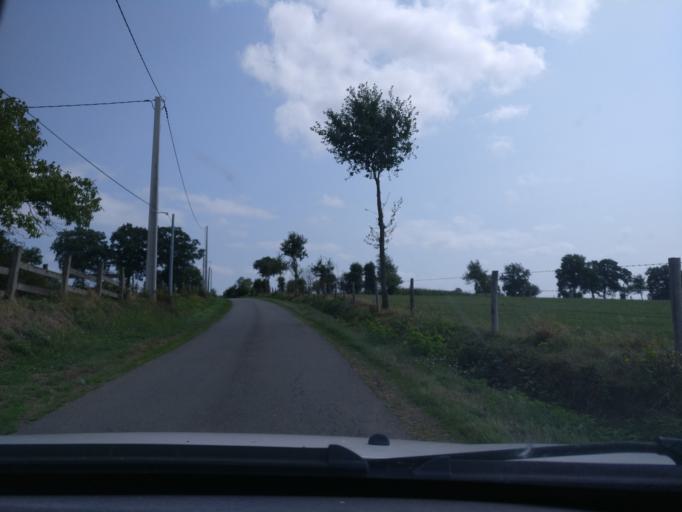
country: FR
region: Brittany
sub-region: Departement d'Ille-et-Vilaine
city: Erce-pres-Liffre
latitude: 48.2676
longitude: -1.5298
